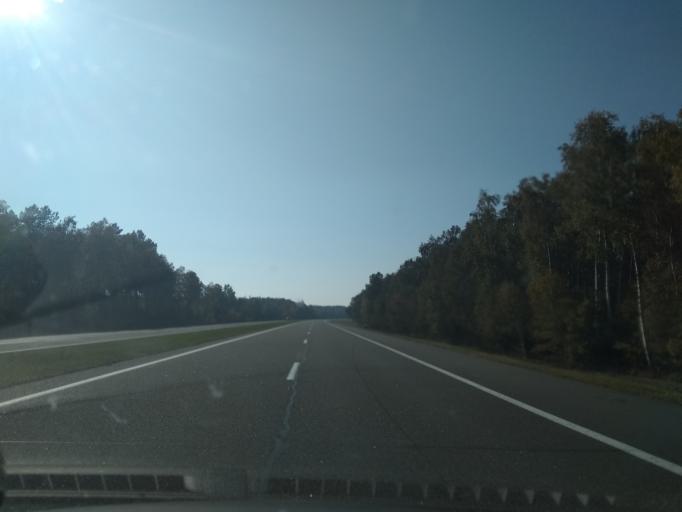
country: BY
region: Brest
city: Antopal'
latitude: 52.3706
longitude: 24.7426
